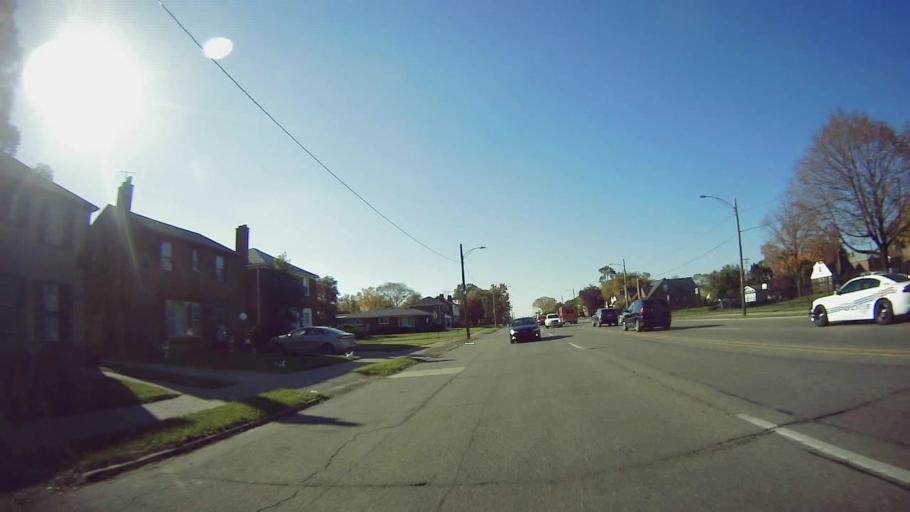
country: US
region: Michigan
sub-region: Oakland County
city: Ferndale
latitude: 42.4313
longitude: -83.1549
